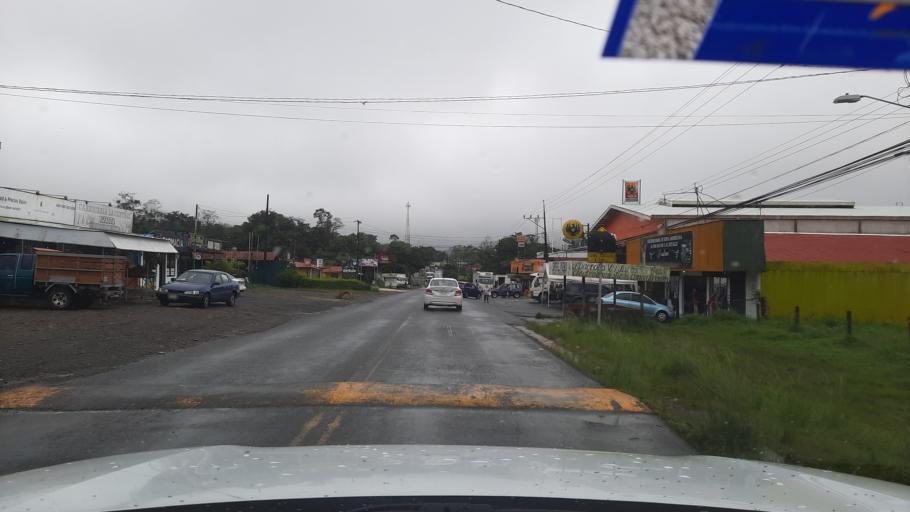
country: CR
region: Alajuela
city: Bijagua
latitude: 10.7323
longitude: -85.0538
